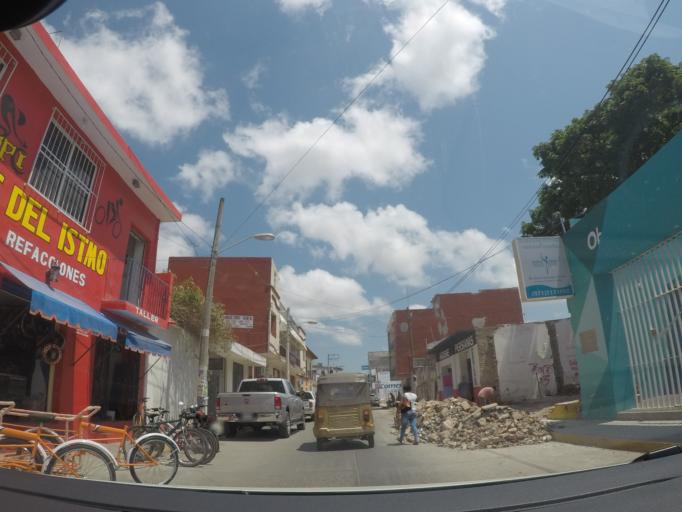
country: MX
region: Oaxaca
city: Juchitan de Zaragoza
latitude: 16.4367
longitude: -95.0223
